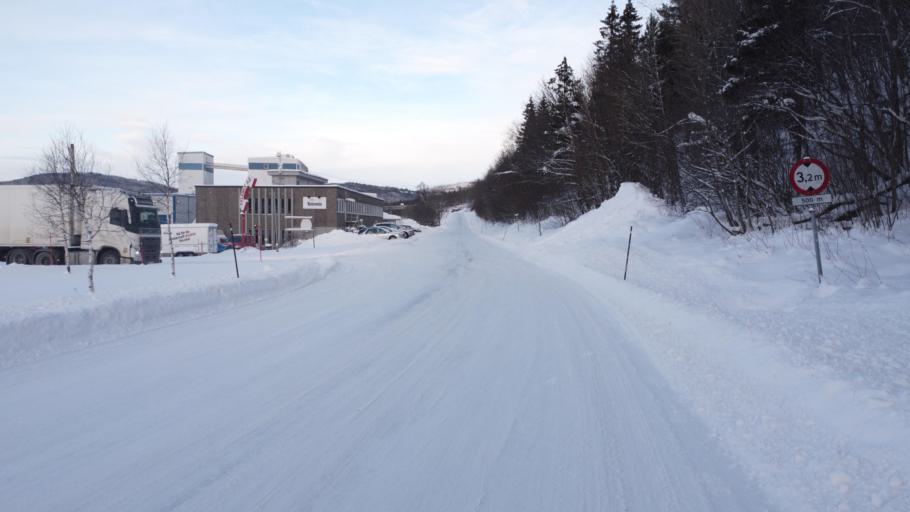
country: NO
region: Nordland
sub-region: Rana
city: Mo i Rana
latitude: 66.3211
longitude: 14.1548
